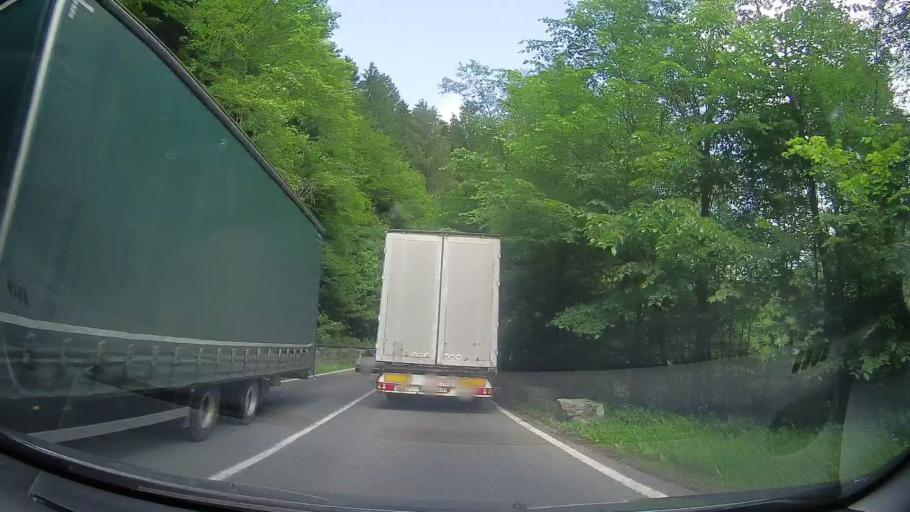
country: RO
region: Prahova
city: Maneciu
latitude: 45.3680
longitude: 25.9298
